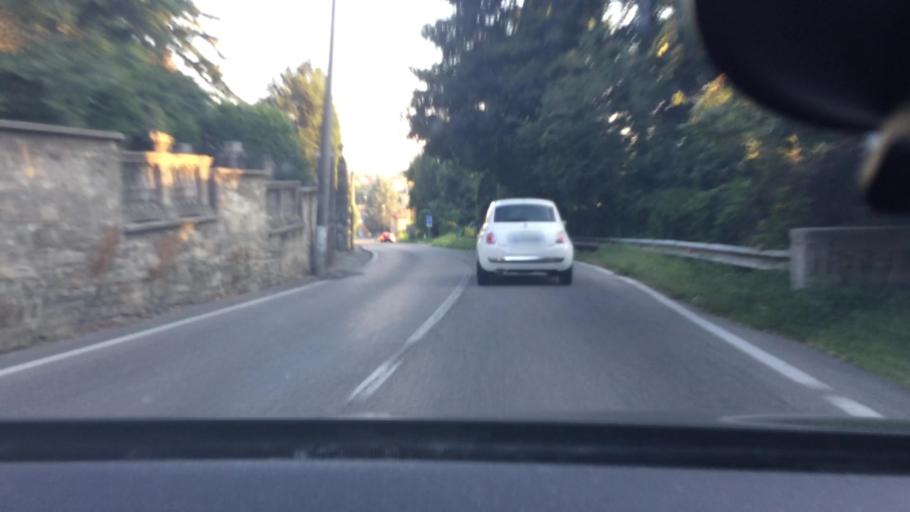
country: IT
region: Lombardy
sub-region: Provincia di Como
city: Cadorago-Caslino al Piano
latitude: 45.7340
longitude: 9.0421
